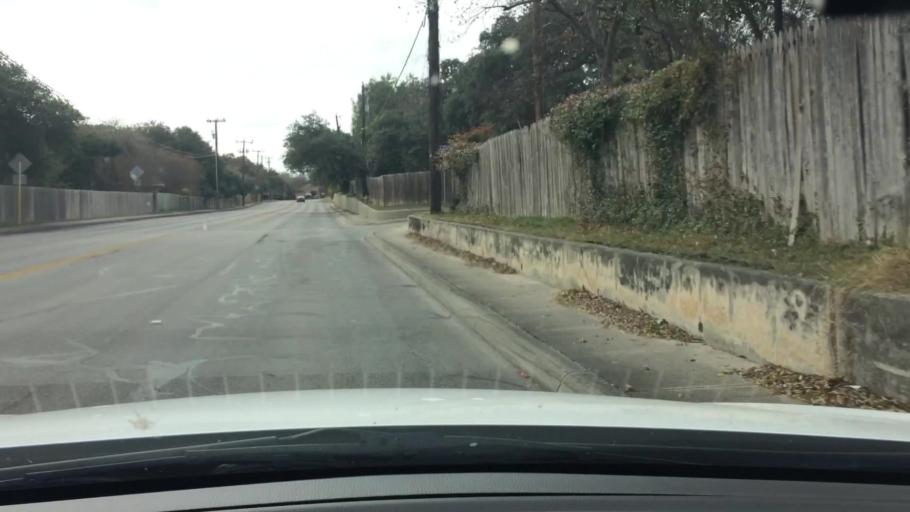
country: US
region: Texas
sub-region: Bexar County
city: Hollywood Park
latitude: 29.5754
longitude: -98.4632
